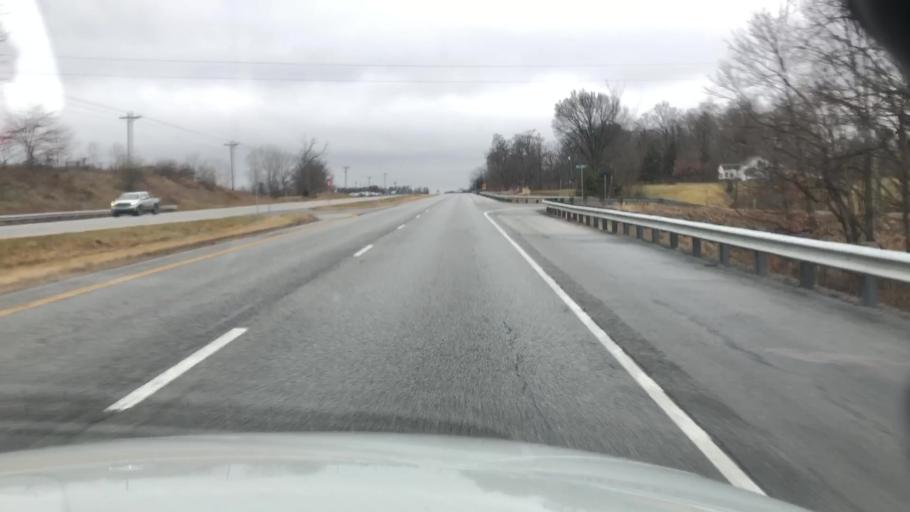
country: US
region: Indiana
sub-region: Whitley County
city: Columbia City
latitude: 41.1764
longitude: -85.5627
